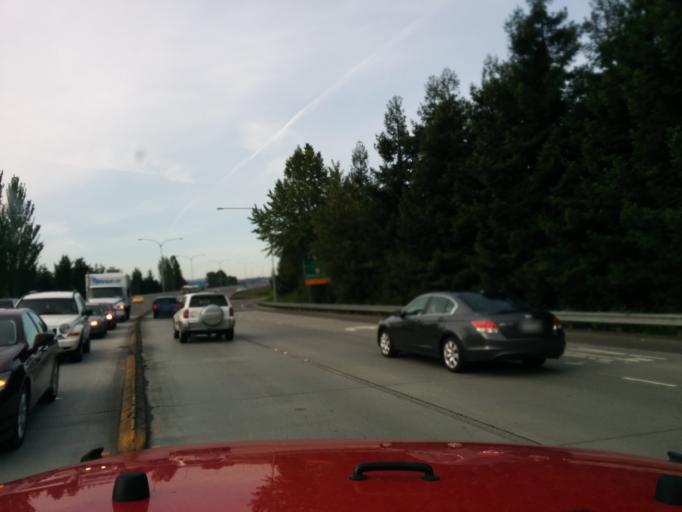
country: US
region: Washington
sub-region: King County
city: Redmond
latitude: 47.6748
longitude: -122.1059
